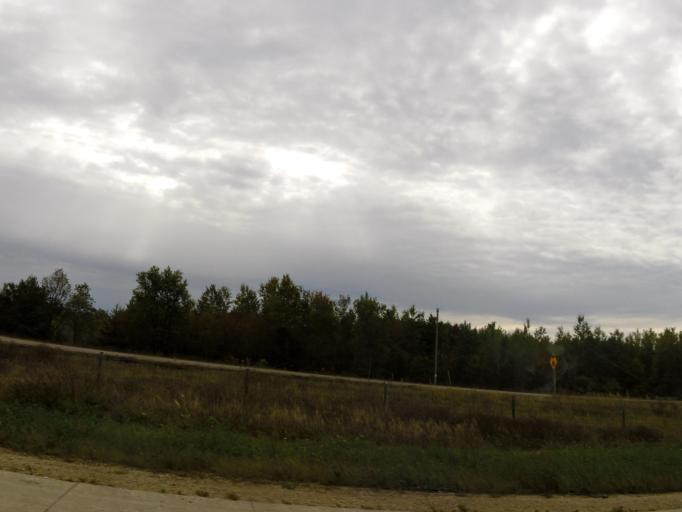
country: US
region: Wisconsin
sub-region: Monroe County
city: Sparta
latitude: 43.9337
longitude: -90.7773
